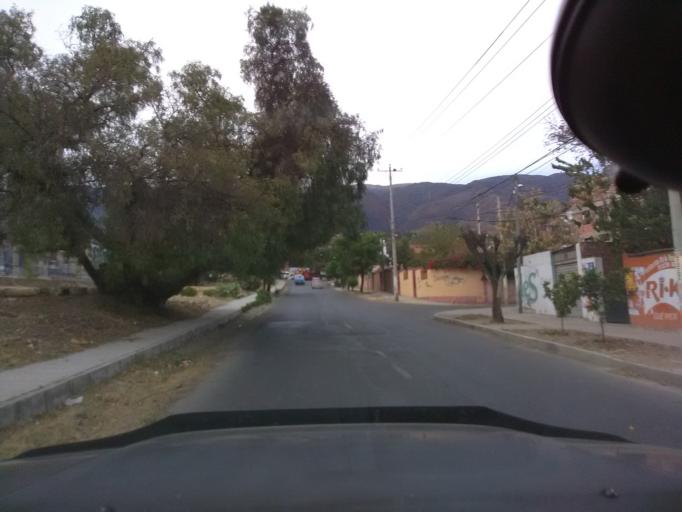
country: BO
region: Cochabamba
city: Cochabamba
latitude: -17.3684
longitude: -66.1492
